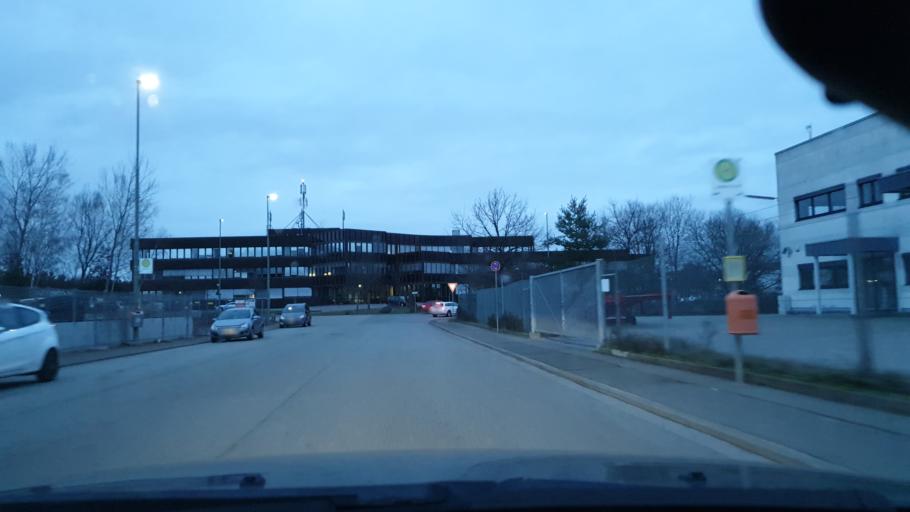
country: DE
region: Rheinland-Pfalz
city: Rodenbach
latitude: 49.4382
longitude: 7.6659
